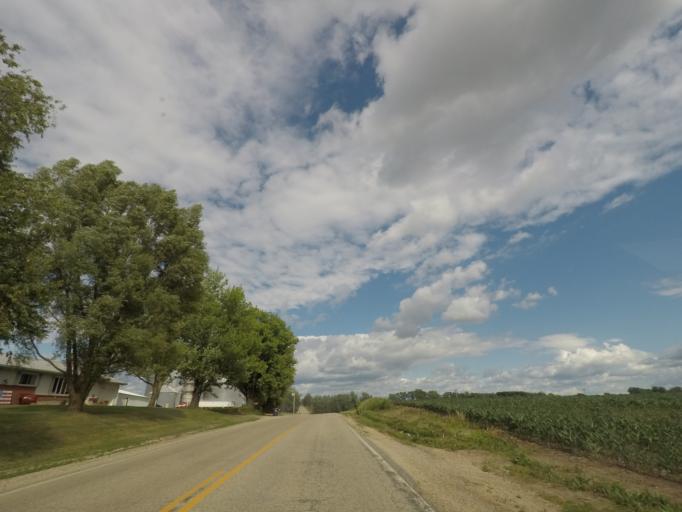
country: US
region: Wisconsin
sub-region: Rock County
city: Orfordville
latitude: 42.7060
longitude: -89.1674
